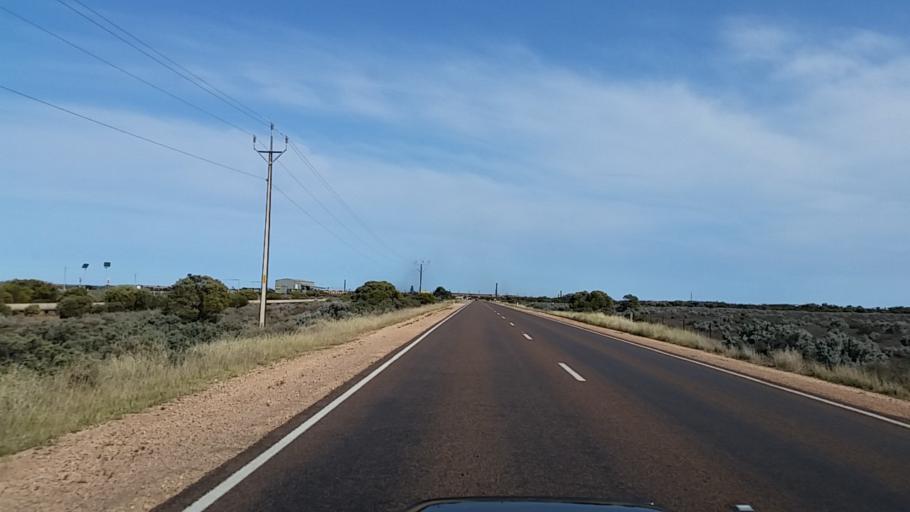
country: AU
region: South Australia
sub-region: Whyalla
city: Whyalla
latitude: -32.9743
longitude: 137.5800
